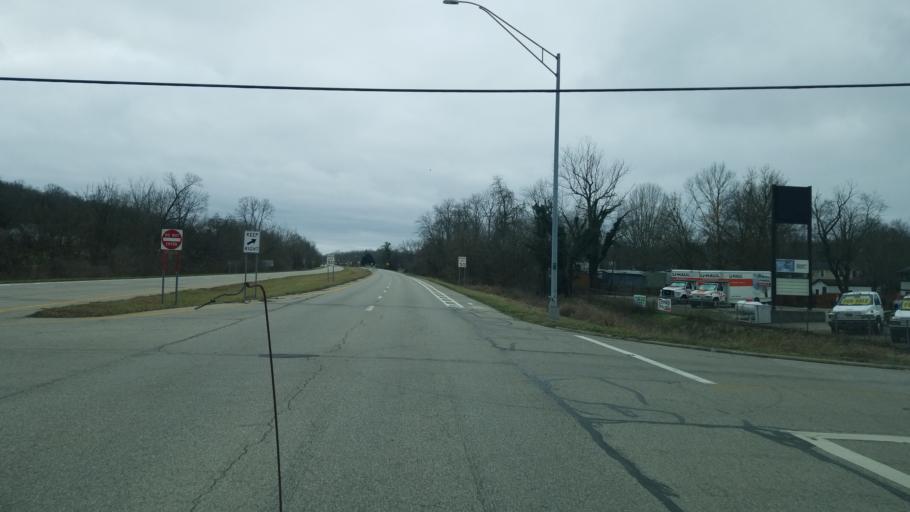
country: US
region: Ohio
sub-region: Clermont County
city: New Richmond
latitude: 38.9532
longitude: -84.2799
